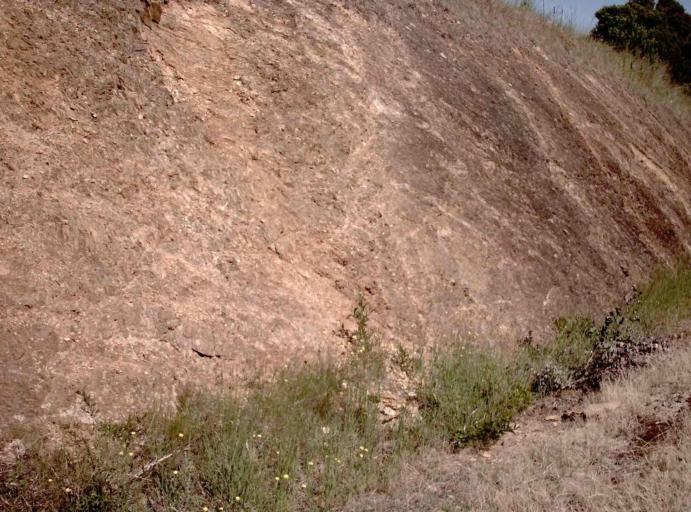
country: AU
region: New South Wales
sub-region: Bombala
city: Bombala
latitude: -37.1678
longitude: 148.7199
